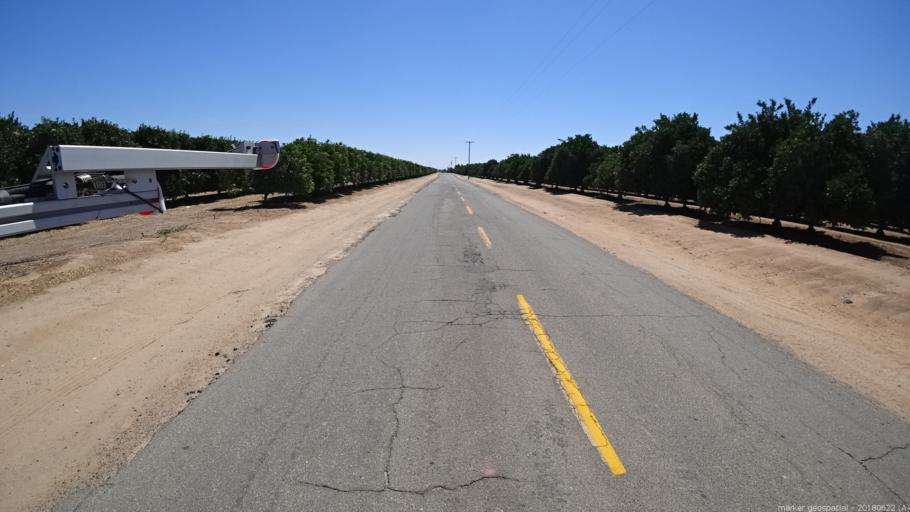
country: US
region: California
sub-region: Madera County
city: Bonadelle Ranchos-Madera Ranchos
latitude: 36.8949
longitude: -119.8482
